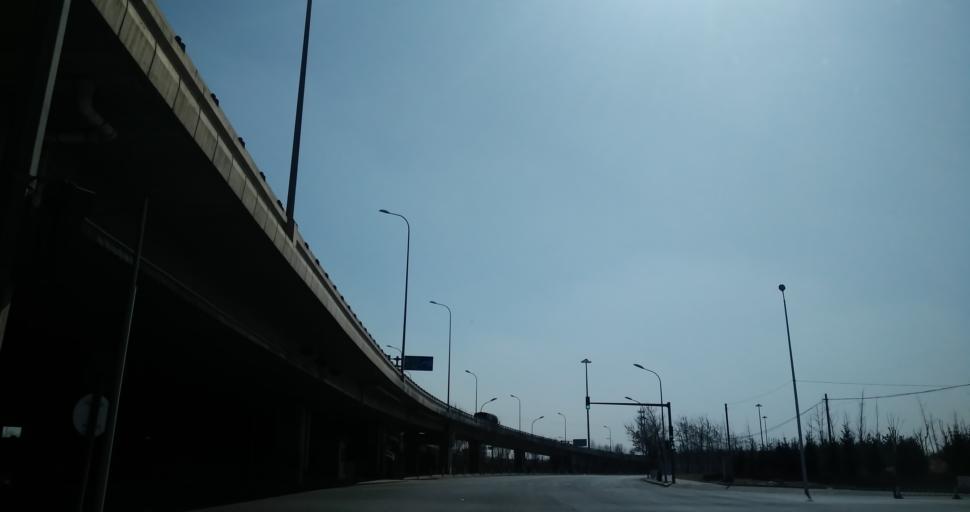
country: CN
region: Beijing
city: Yinghai
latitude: 39.7876
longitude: 116.4242
